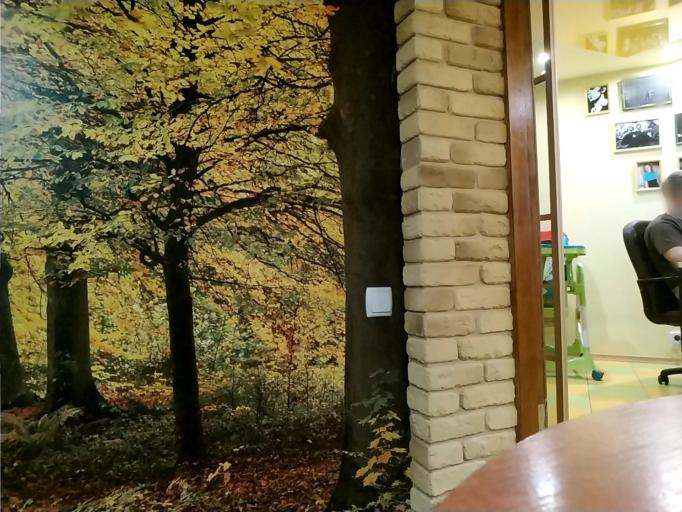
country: RU
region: Tverskaya
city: Zapadnaya Dvina
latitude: 56.3302
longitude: 31.8906
